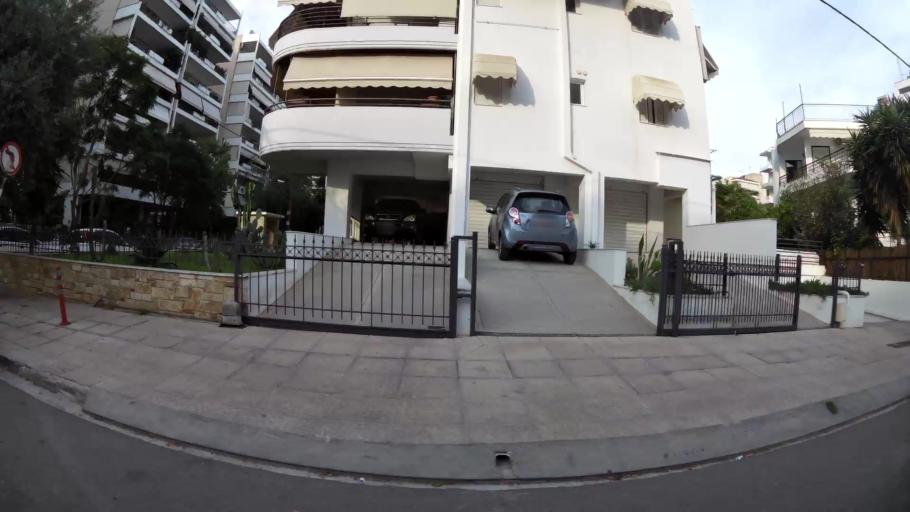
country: GR
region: Attica
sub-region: Nomarchia Athinas
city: Palaio Faliro
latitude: 37.9335
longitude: 23.6978
